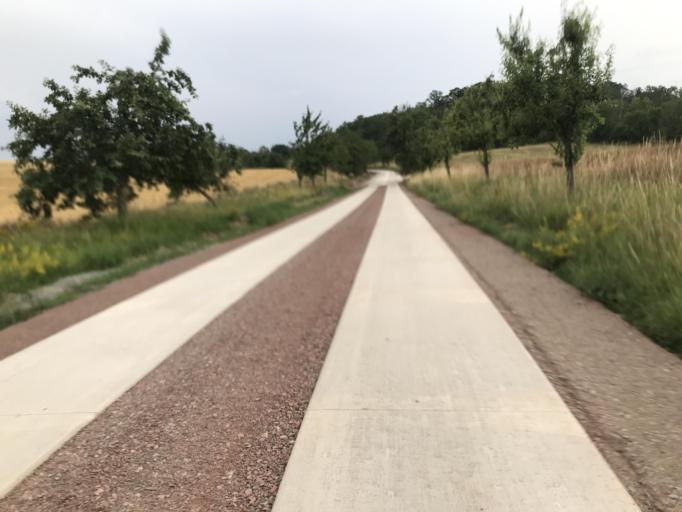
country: DE
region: Saxony-Anhalt
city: Harsleben
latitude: 51.8623
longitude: 11.0872
